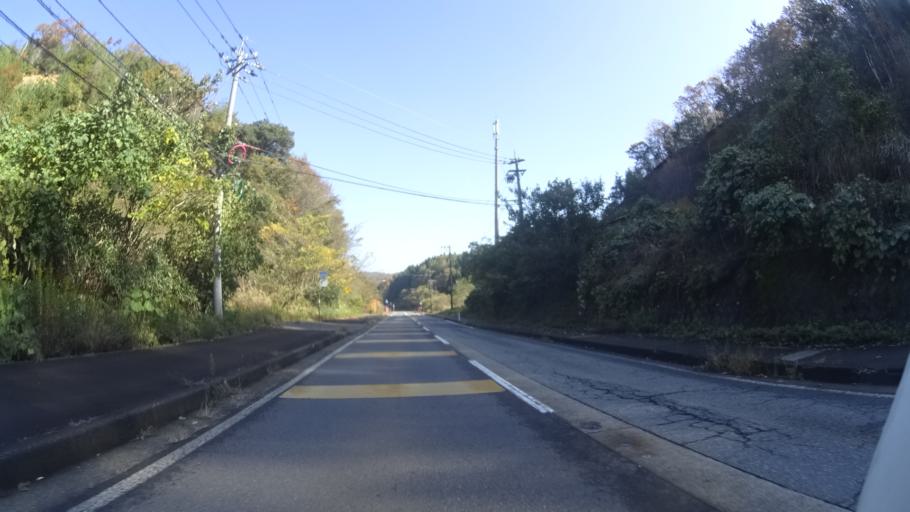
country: JP
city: Asahi
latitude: 35.9598
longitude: 136.0710
